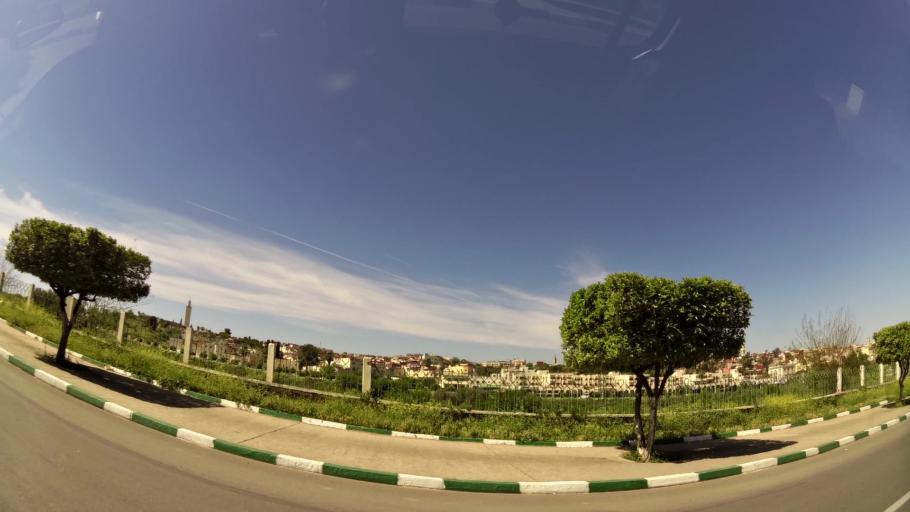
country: MA
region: Meknes-Tafilalet
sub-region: Meknes
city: Meknes
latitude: 33.8946
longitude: -5.5537
